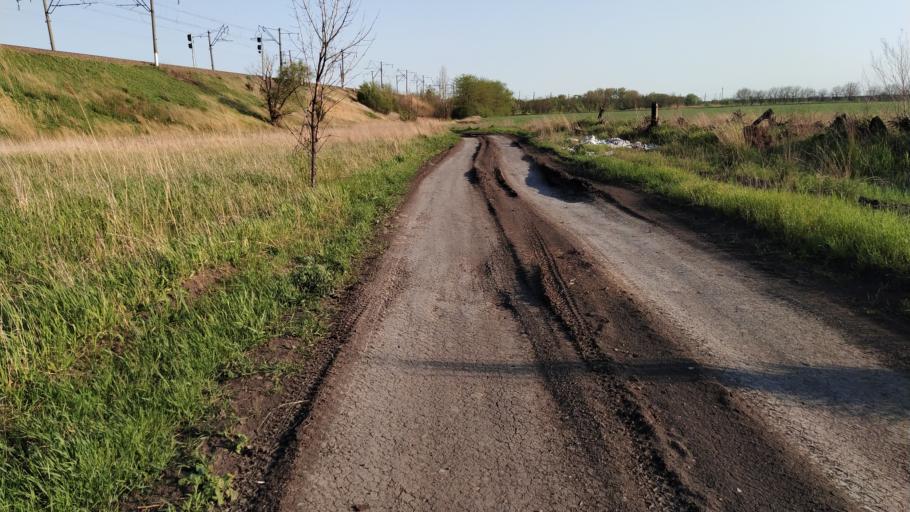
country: RU
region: Rostov
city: Bataysk
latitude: 47.0924
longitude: 39.7124
